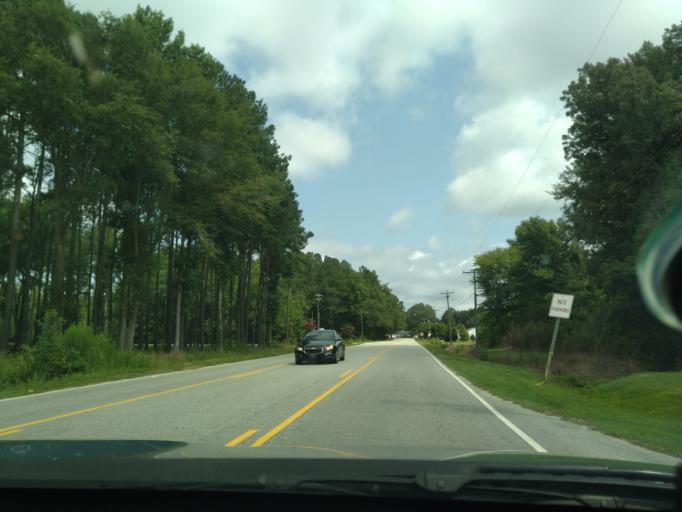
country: US
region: North Carolina
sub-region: Edgecombe County
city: Princeville
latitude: 35.8742
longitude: -77.5228
